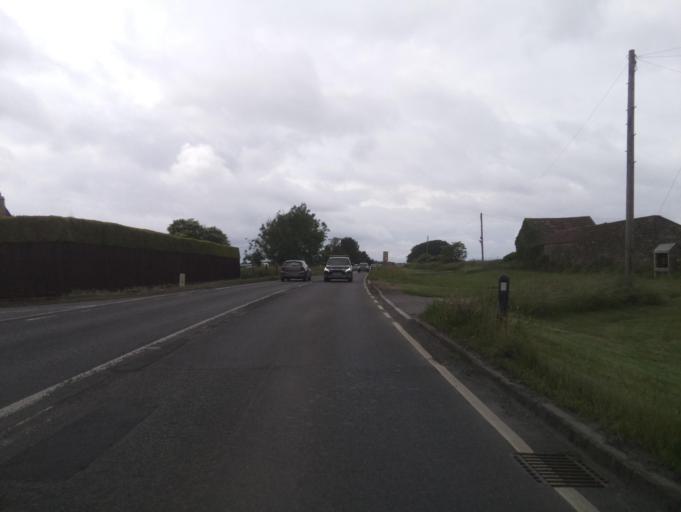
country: GB
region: England
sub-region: South Gloucestershire
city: Cold Ashton
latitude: 51.4162
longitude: -2.3954
